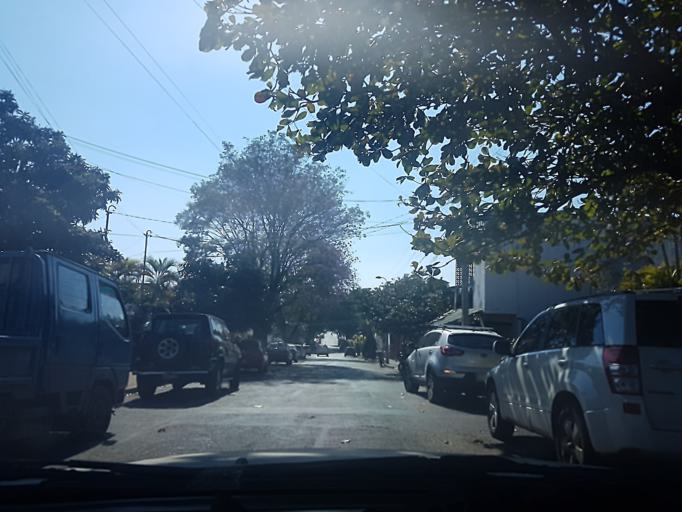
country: PY
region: Asuncion
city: Asuncion
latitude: -25.2984
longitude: -57.6306
